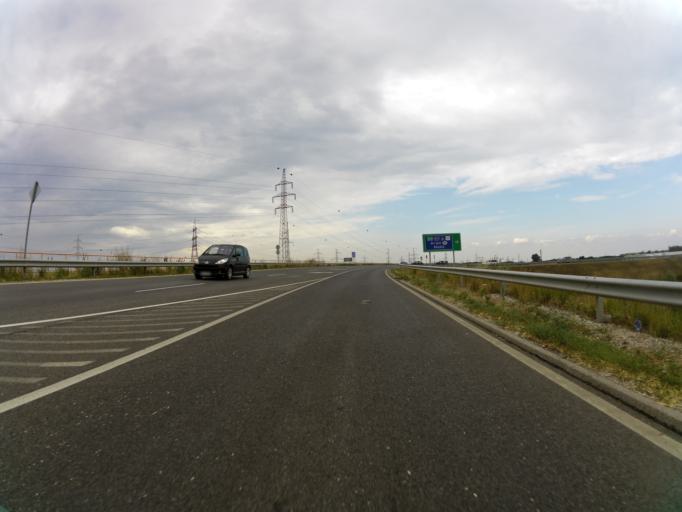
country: HU
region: Csongrad
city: Szeged
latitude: 46.2928
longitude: 20.1353
